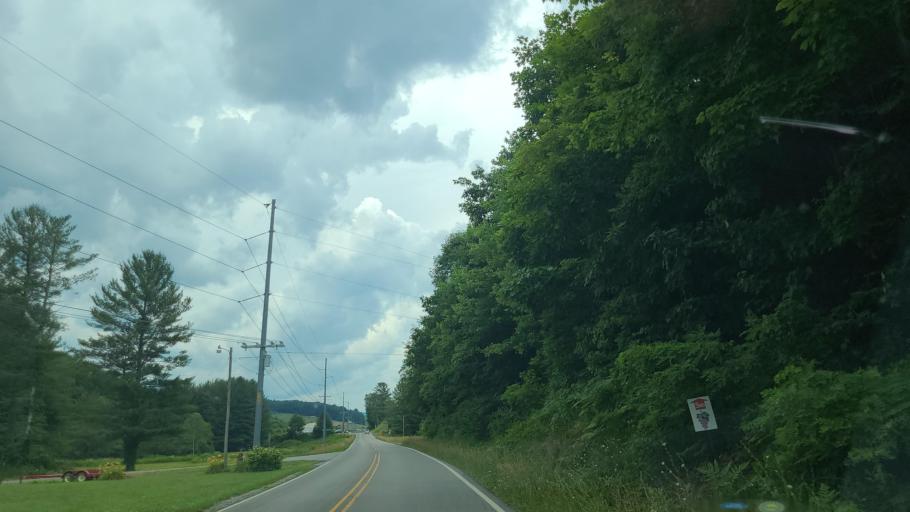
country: US
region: North Carolina
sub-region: Ashe County
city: Jefferson
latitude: 36.3939
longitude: -81.3210
